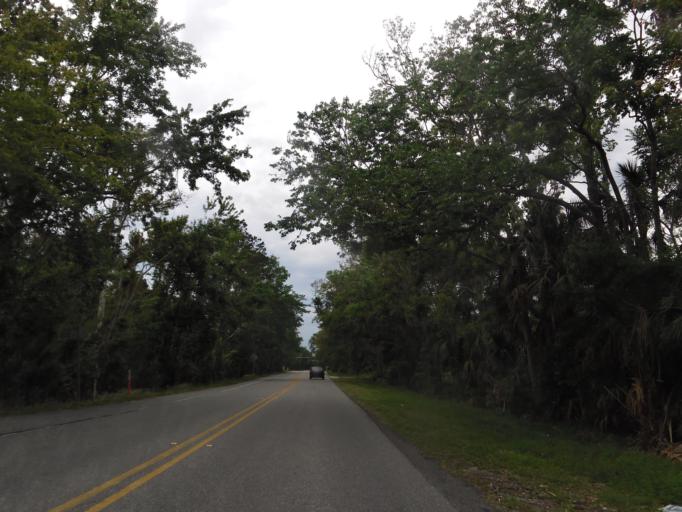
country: US
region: Florida
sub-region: Saint Johns County
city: Ponte Vedra Beach
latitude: 30.2192
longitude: -81.3996
